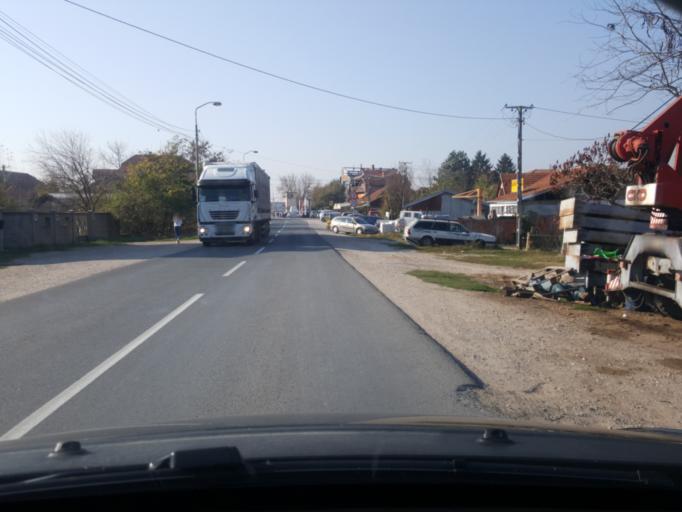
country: RS
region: Central Serbia
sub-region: Nisavski Okrug
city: Nis
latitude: 43.3306
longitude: 21.9500
